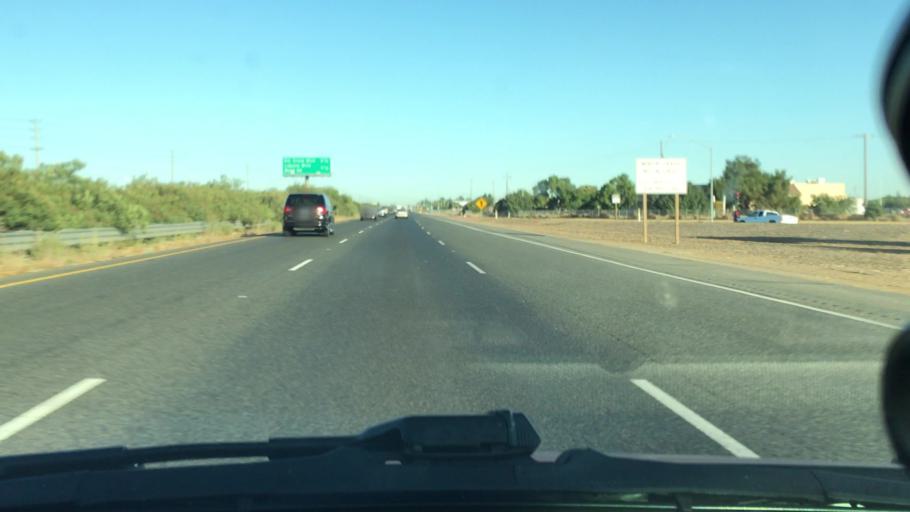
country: US
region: California
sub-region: Sacramento County
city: Elk Grove
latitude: 38.3775
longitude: -121.3630
